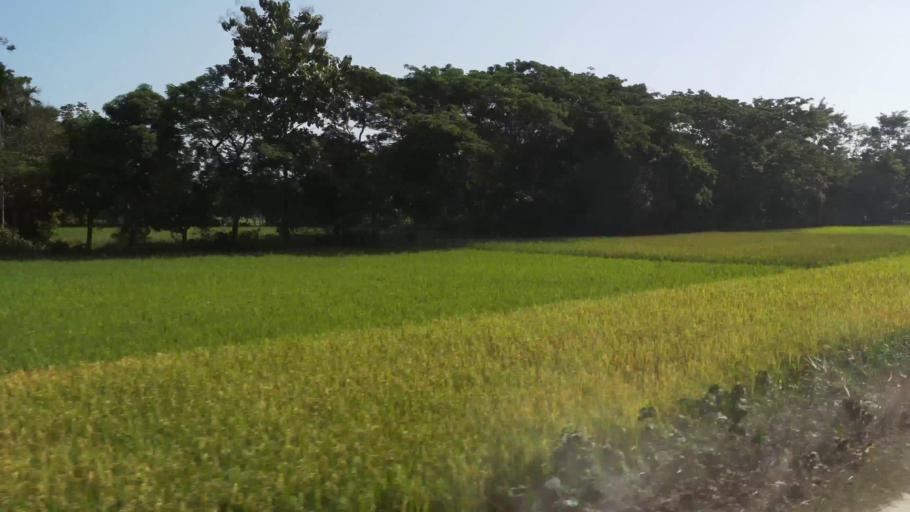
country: BD
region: Dhaka
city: Gafargaon
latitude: 24.5319
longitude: 90.5086
